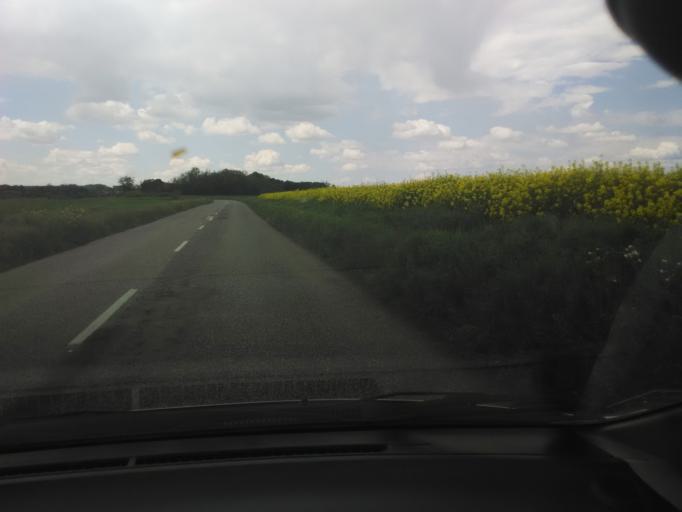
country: SK
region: Nitriansky
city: Levice
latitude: 48.1291
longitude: 18.4814
